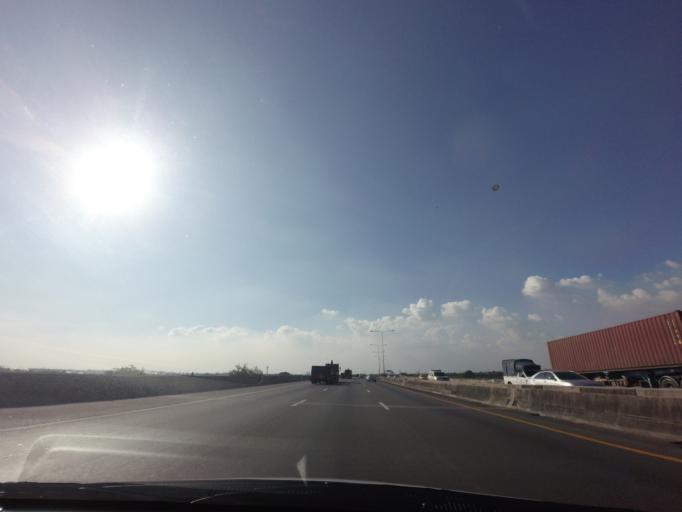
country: TH
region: Samut Prakan
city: Samut Prakan
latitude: 13.6005
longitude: 100.6411
